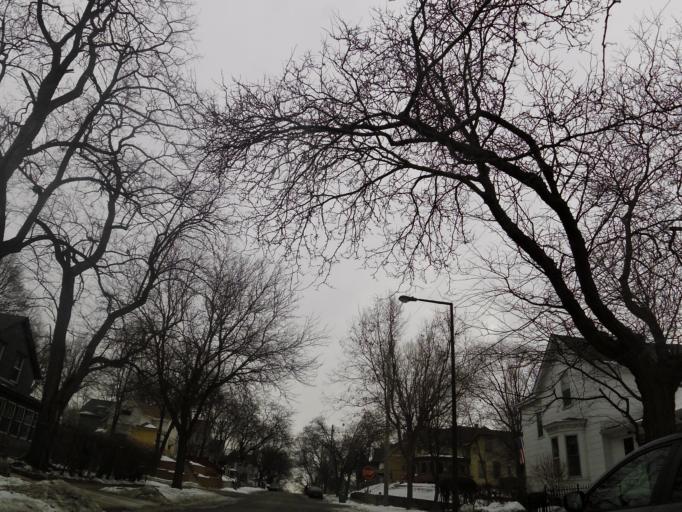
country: US
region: Minnesota
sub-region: Ramsey County
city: Saint Paul
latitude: 44.9582
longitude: -93.0686
